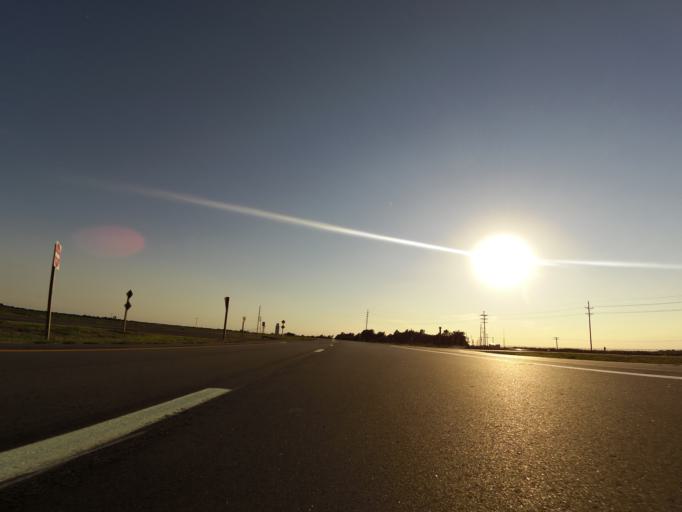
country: US
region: Kansas
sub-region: Reno County
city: South Hutchinson
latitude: 38.0135
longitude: -98.0015
